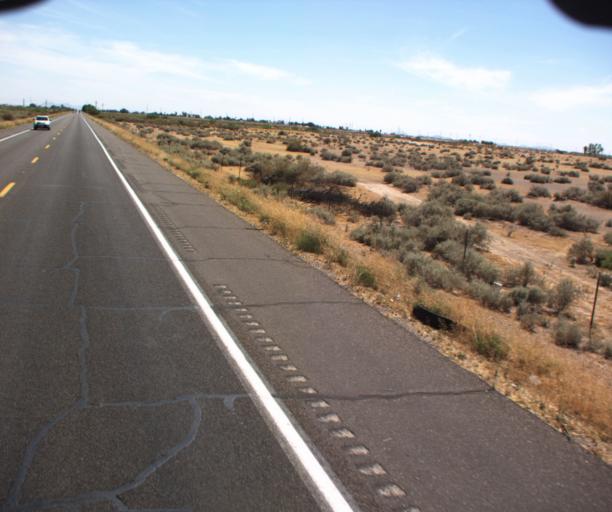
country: US
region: Arizona
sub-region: Pinal County
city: Coolidge
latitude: 32.8994
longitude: -111.5151
